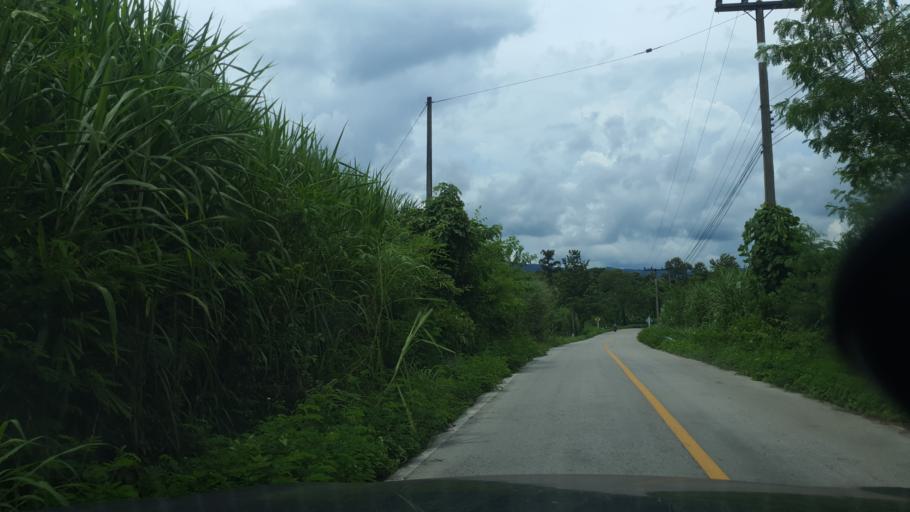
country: TH
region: Lampang
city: Hang Chat
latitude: 18.3955
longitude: 99.2647
